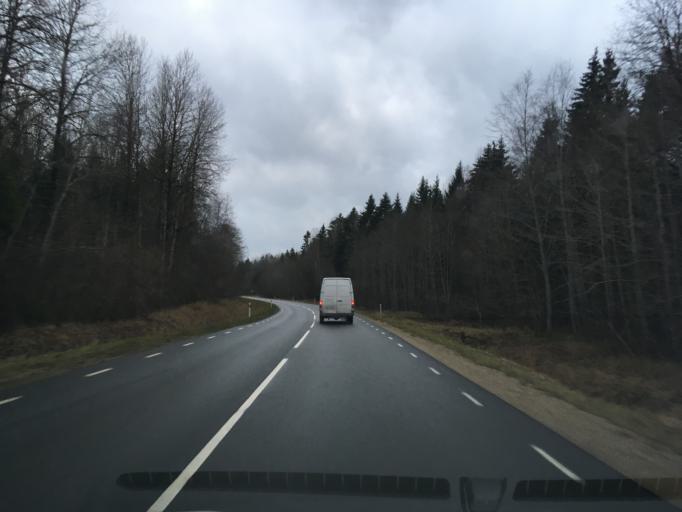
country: EE
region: Harju
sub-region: Anija vald
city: Kehra
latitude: 59.2730
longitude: 25.3580
